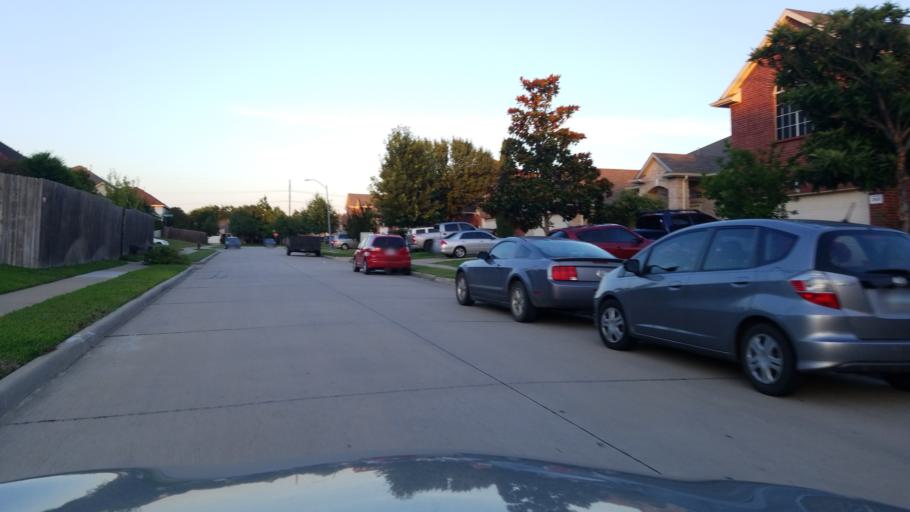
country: US
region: Texas
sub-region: Dallas County
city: Grand Prairie
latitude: 32.6846
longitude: -97.0387
